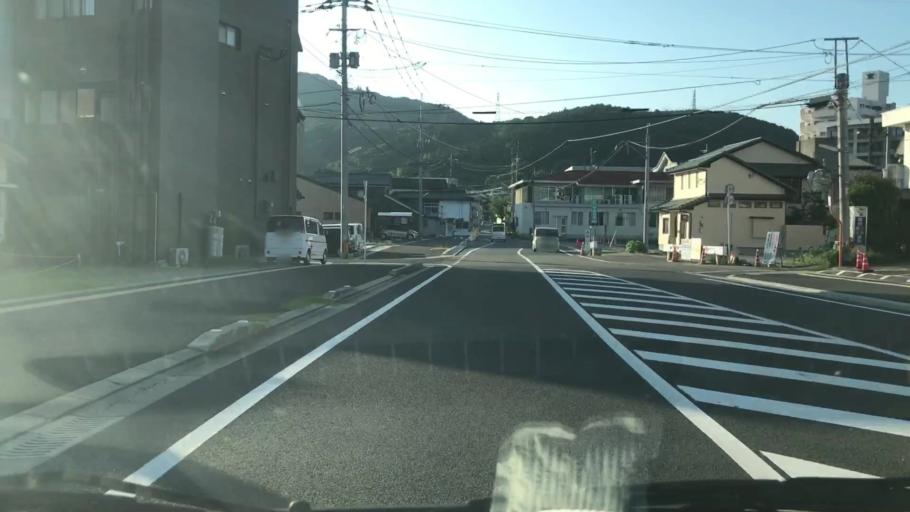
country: JP
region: Saga Prefecture
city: Takeocho-takeo
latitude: 33.1951
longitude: 130.0204
